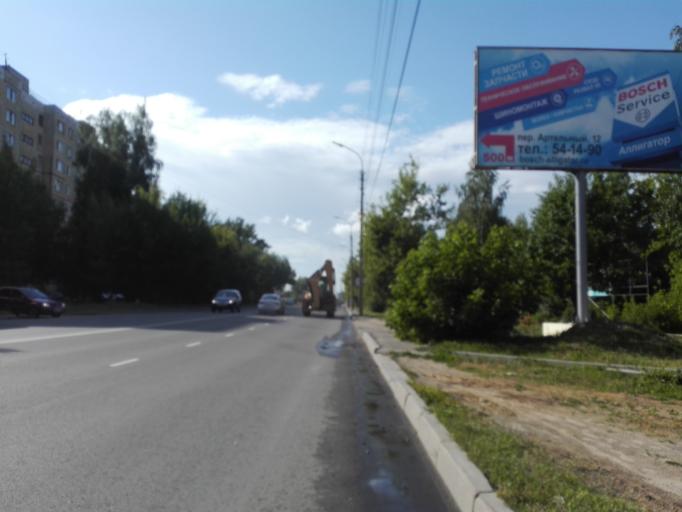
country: RU
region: Orjol
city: Orel
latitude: 52.9911
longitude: 36.1172
